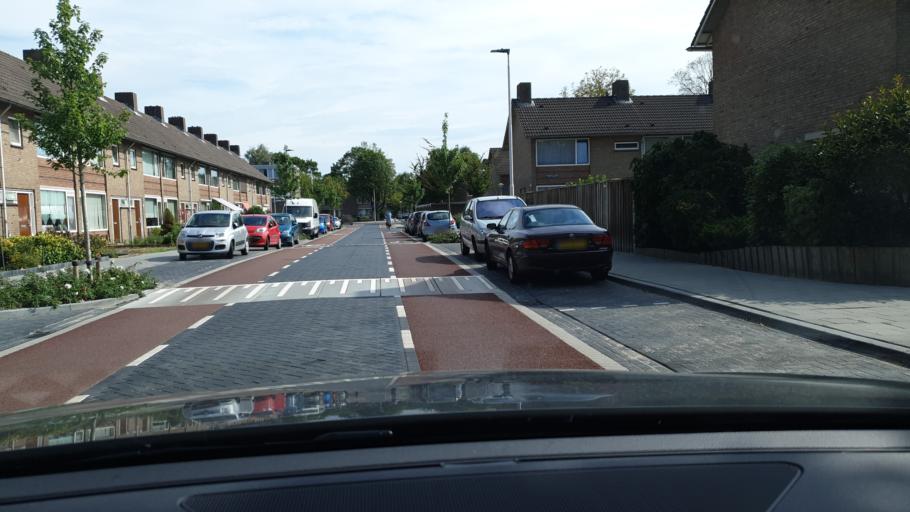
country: NL
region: North Brabant
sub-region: Gemeente Eindhoven
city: Eindhoven
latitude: 51.4757
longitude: 5.4667
